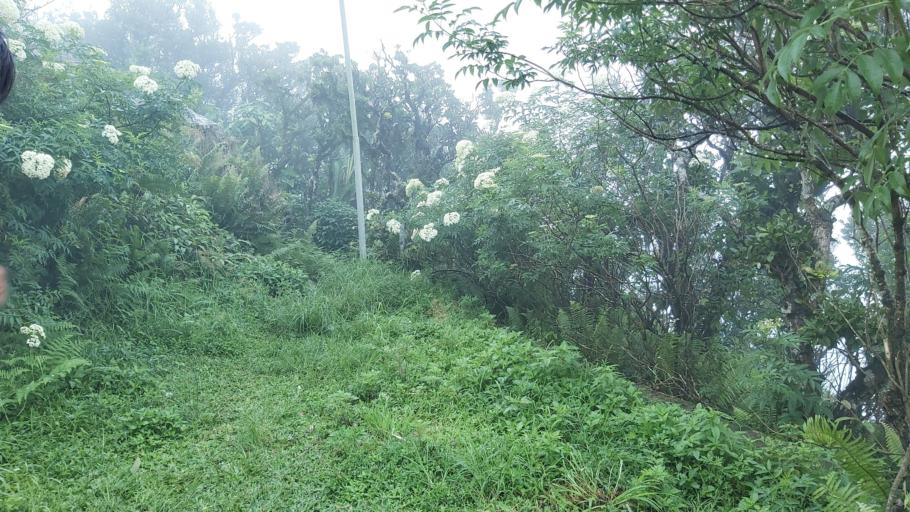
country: KH
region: Kampot
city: Kampot
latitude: 10.6300
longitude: 104.0171
